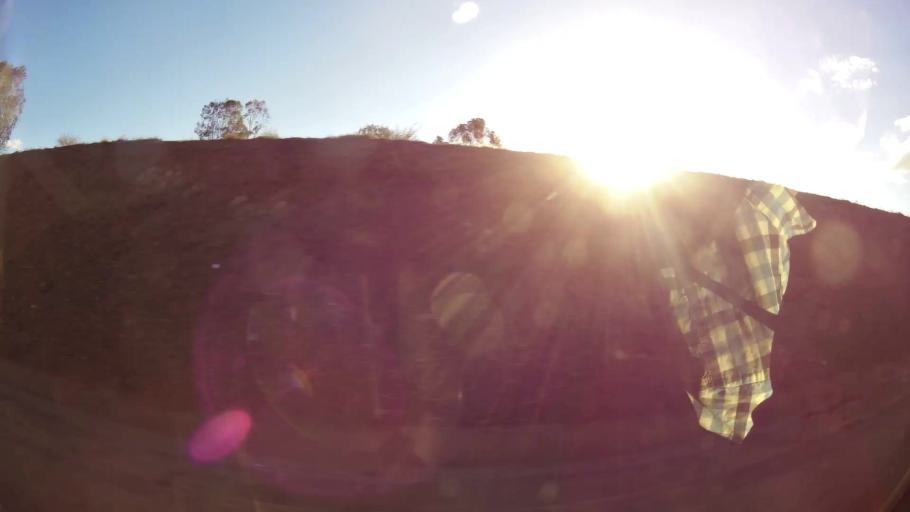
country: ZA
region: Western Cape
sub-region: Eden District Municipality
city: Riversdale
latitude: -34.1009
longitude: 20.9597
